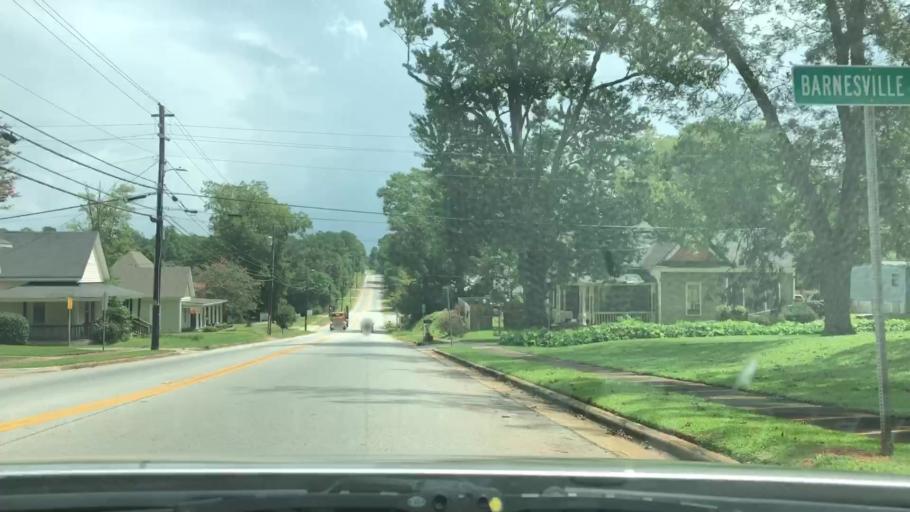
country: US
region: Georgia
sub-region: Pike County
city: Zebulon
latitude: 33.1021
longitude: -84.3411
